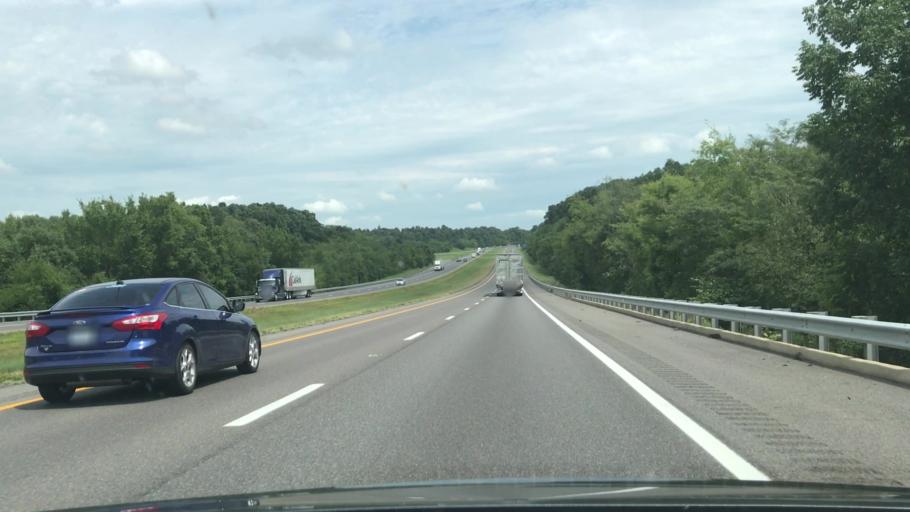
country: US
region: Kentucky
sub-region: Lyon County
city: Eddyville
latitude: 37.0611
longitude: -88.2127
